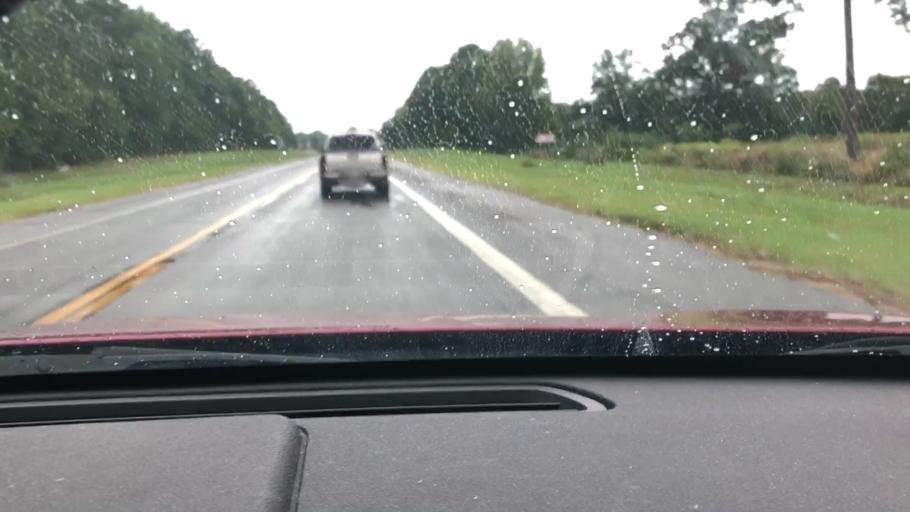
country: US
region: Arkansas
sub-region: Columbia County
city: Magnolia
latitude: 33.2969
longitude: -93.2437
